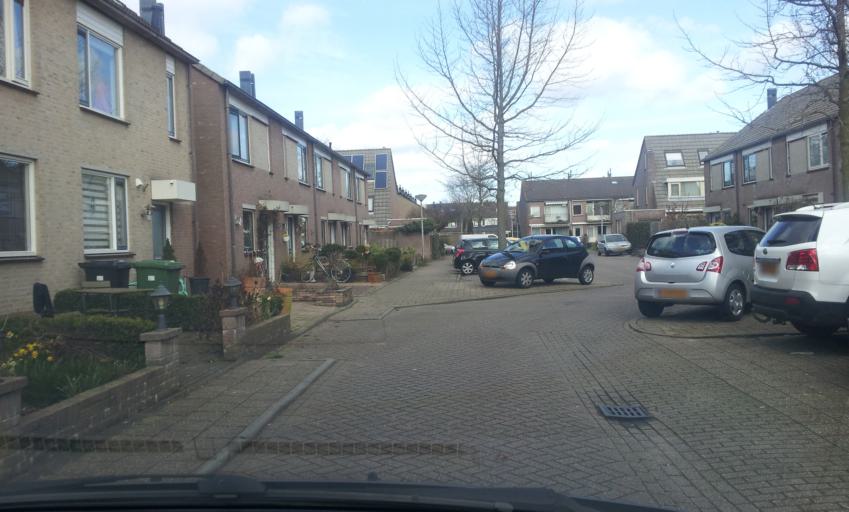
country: NL
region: South Holland
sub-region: Gemeente Den Haag
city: Ypenburg
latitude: 52.0422
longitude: 4.3989
